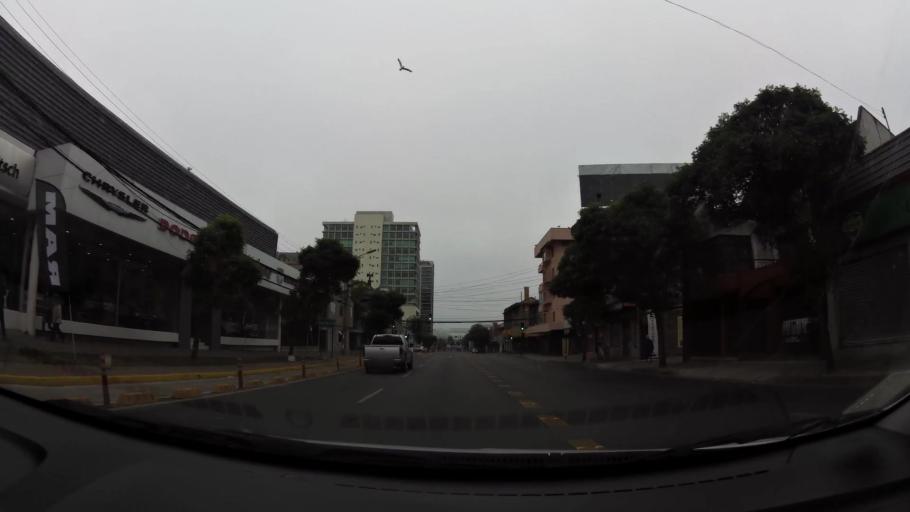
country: CL
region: Biobio
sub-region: Provincia de Concepcion
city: Concepcion
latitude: -36.8302
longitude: -73.0562
